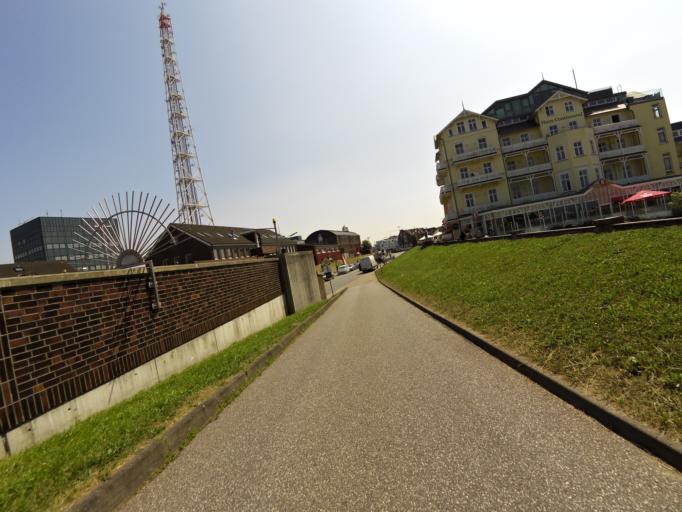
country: DE
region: Lower Saxony
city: Cuxhaven
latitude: 53.8705
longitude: 8.7063
